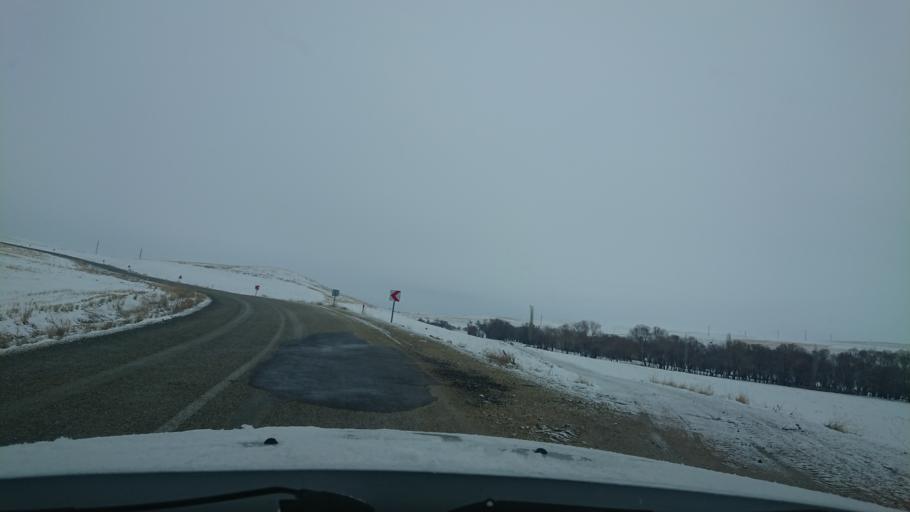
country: TR
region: Aksaray
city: Agacoren
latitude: 38.7612
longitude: 33.8705
